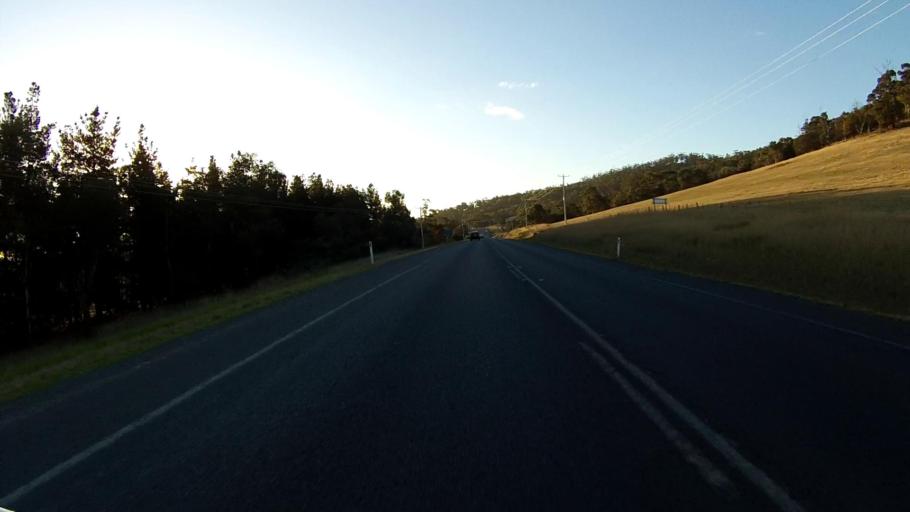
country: AU
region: Tasmania
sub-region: Sorell
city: Sorell
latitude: -42.7924
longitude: 147.6074
